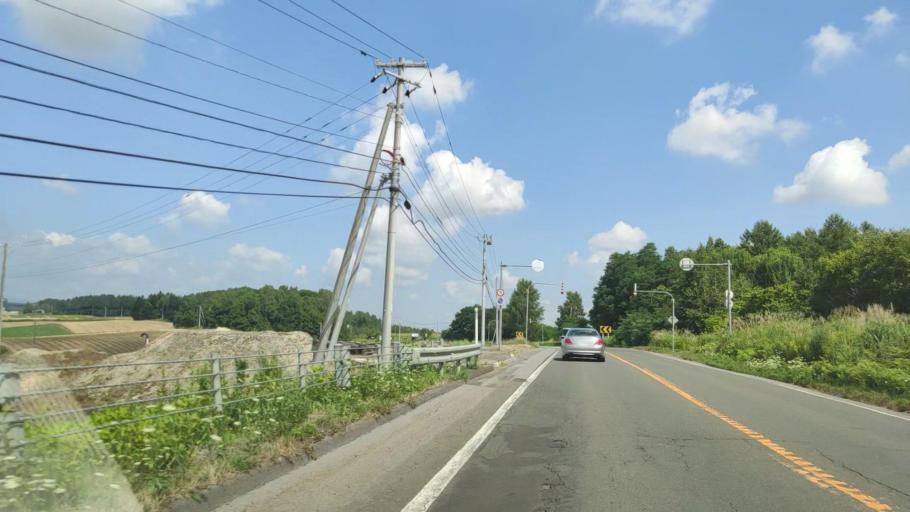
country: JP
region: Hokkaido
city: Shimo-furano
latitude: 43.5042
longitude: 142.4588
